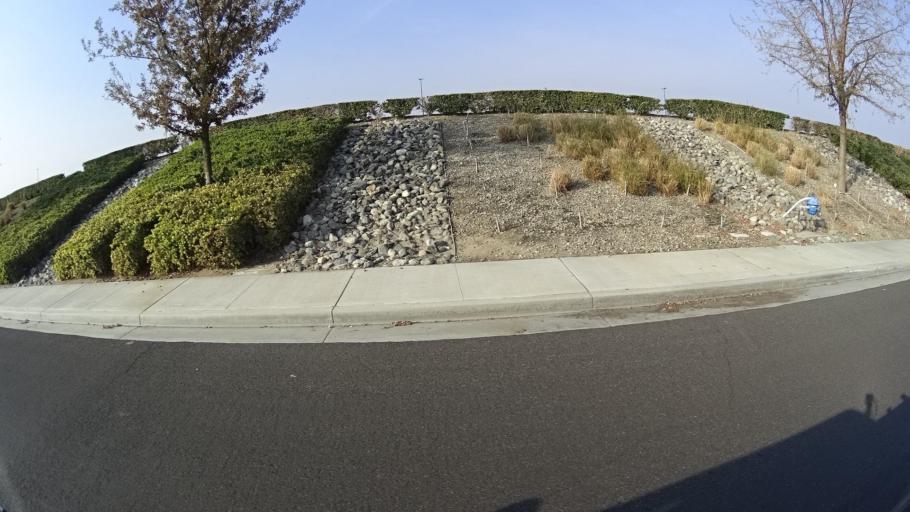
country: US
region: California
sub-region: Kern County
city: Lebec
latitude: 34.9876
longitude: -118.9397
